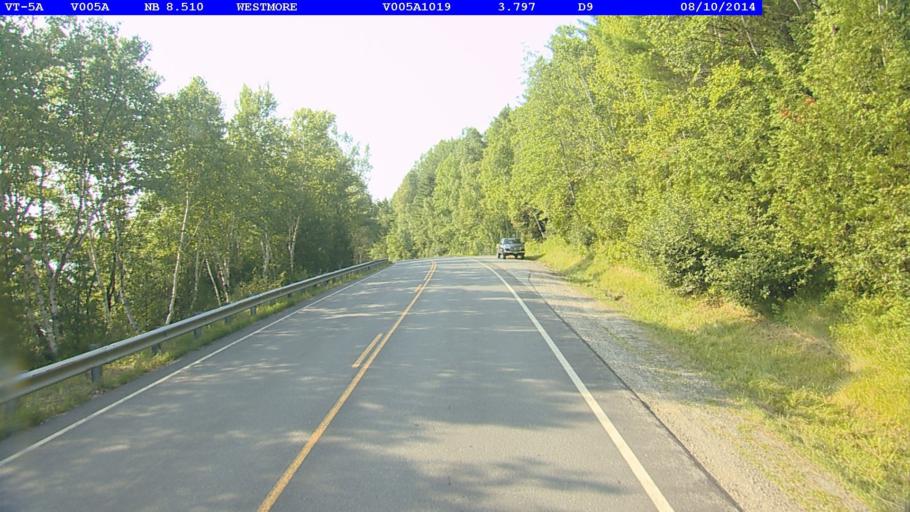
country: US
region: Vermont
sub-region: Caledonia County
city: Lyndonville
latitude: 44.7456
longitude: -72.0493
